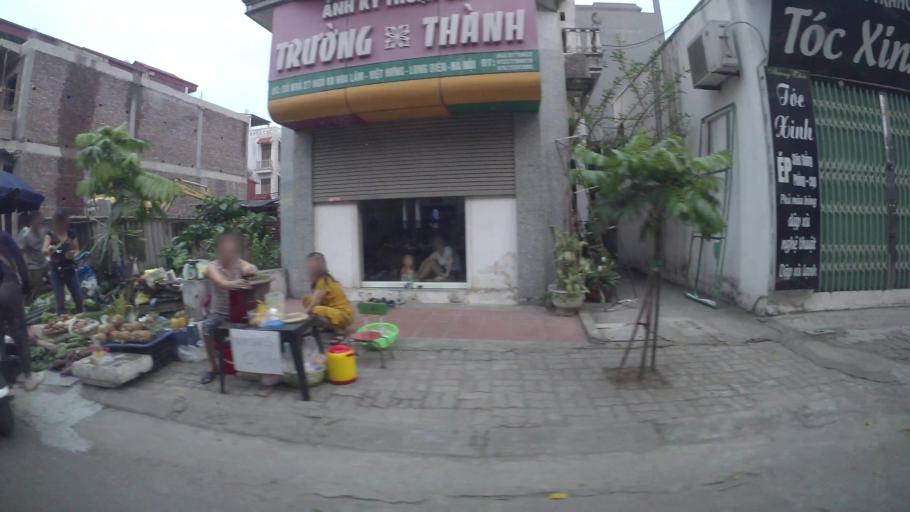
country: VN
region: Ha Noi
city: Hoan Kiem
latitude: 21.0555
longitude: 105.8945
